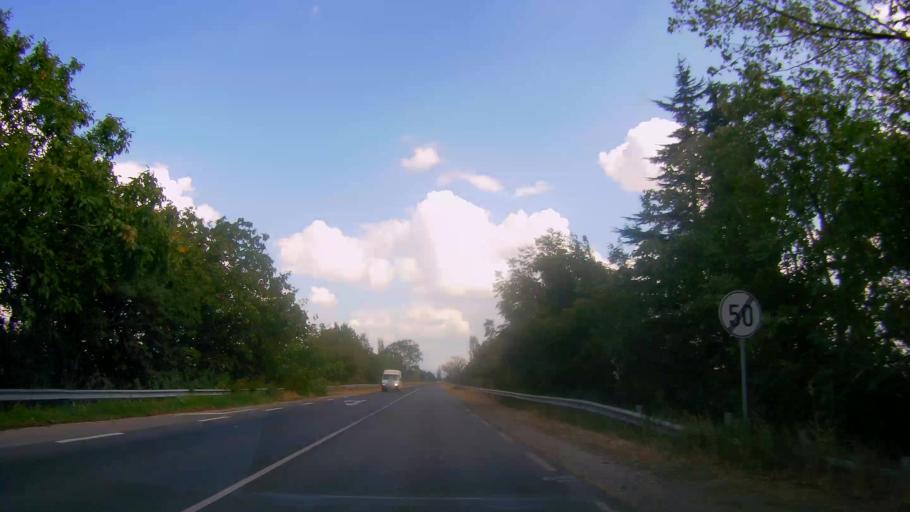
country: BG
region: Sliven
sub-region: Obshtina Sliven
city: Sliven
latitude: 42.6355
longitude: 26.2184
